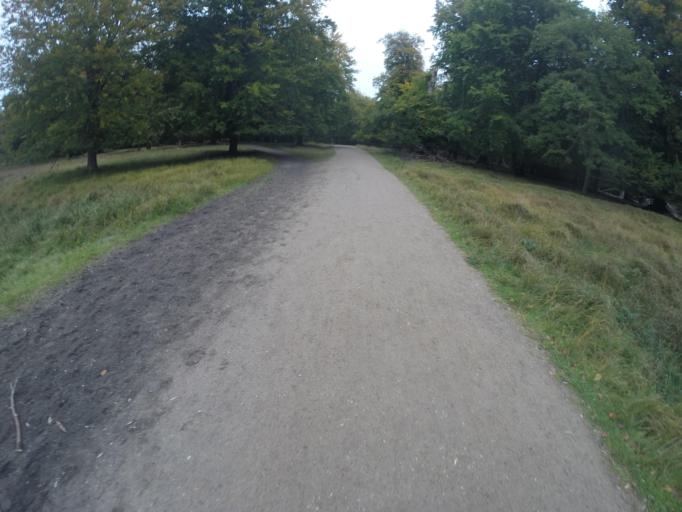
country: DK
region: Capital Region
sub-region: Gentofte Kommune
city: Charlottenlund
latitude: 55.7764
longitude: 12.5671
